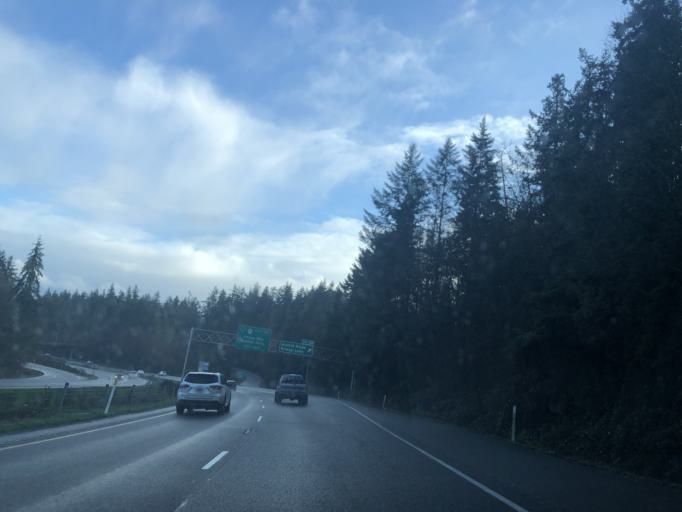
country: US
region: Washington
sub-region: Kitsap County
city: Erlands Point-Kitsap Lake
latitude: 47.5837
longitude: -122.6987
